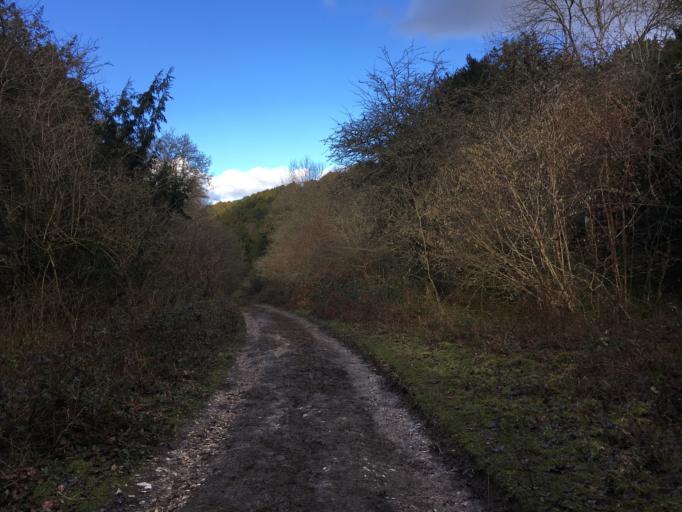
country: GB
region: England
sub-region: Surrey
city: Mickleham
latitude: 51.2561
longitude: -0.3075
